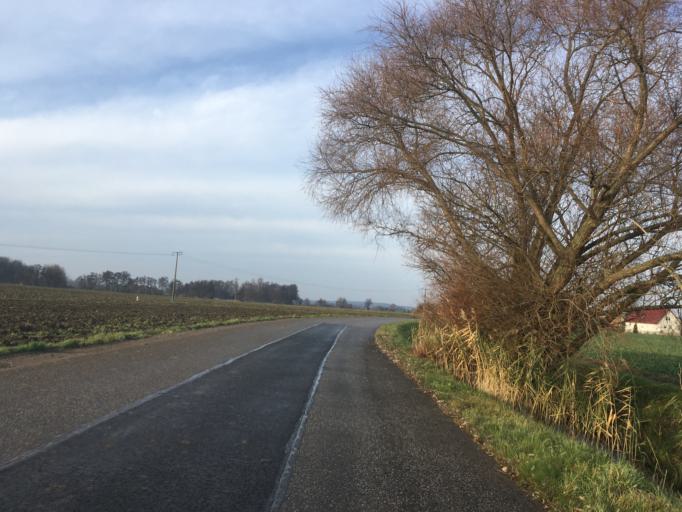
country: DE
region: Brandenburg
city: Bad Freienwalde
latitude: 52.8047
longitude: 14.0123
